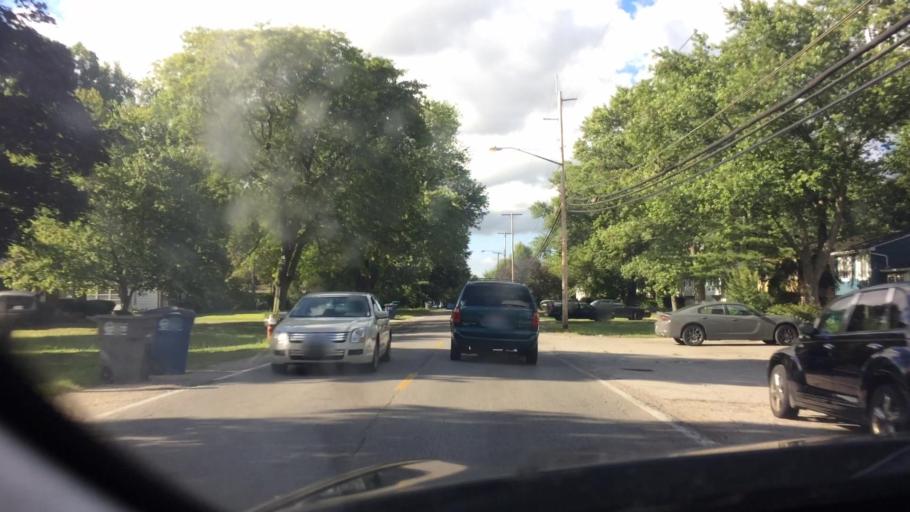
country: US
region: Ohio
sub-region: Lucas County
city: Ottawa Hills
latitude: 41.6429
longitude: -83.6406
